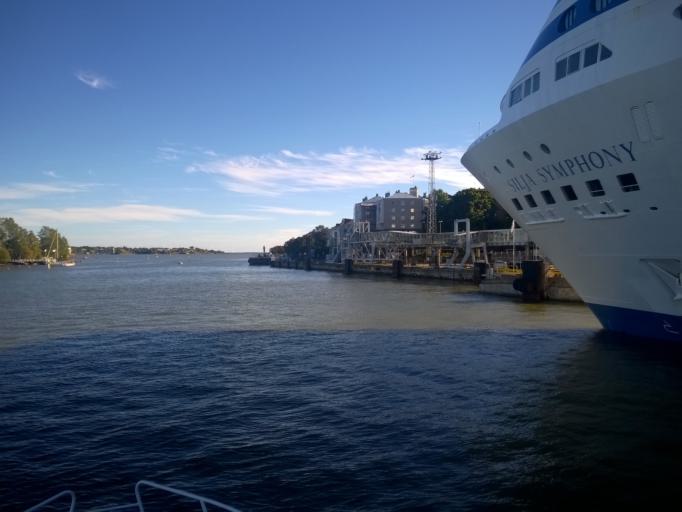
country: FI
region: Uusimaa
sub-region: Helsinki
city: Helsinki
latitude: 60.1617
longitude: 24.9598
